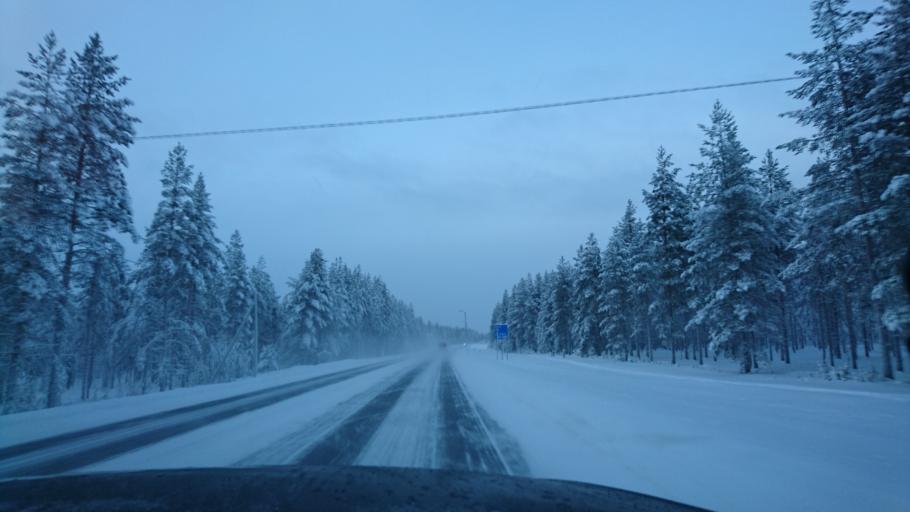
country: FI
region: Kainuu
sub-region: Kehys-Kainuu
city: Puolanka
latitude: 65.4300
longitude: 27.5482
